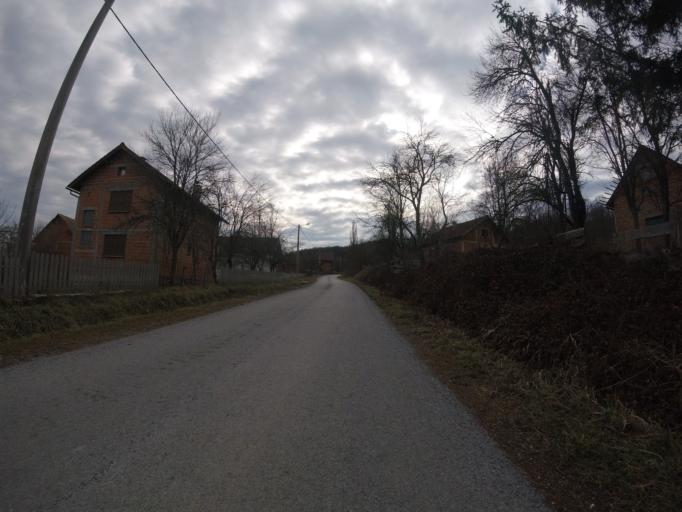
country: HR
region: Sisacko-Moslavacka
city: Glina
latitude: 45.4268
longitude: 16.0904
